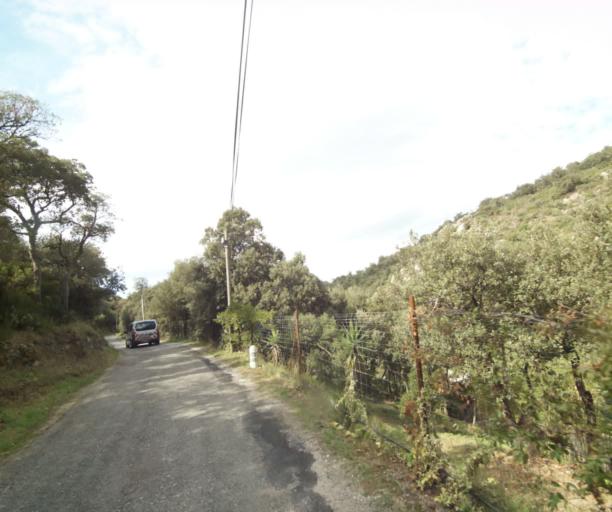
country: FR
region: Languedoc-Roussillon
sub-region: Departement des Pyrenees-Orientales
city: Sorede
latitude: 42.5217
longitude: 2.9902
